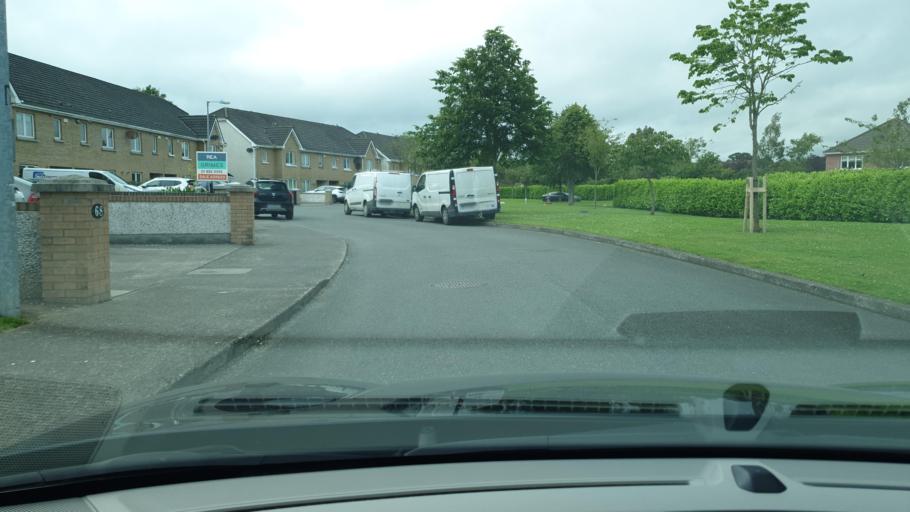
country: IE
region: Leinster
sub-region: An Mhi
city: Ratoath
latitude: 53.5059
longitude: -6.4744
